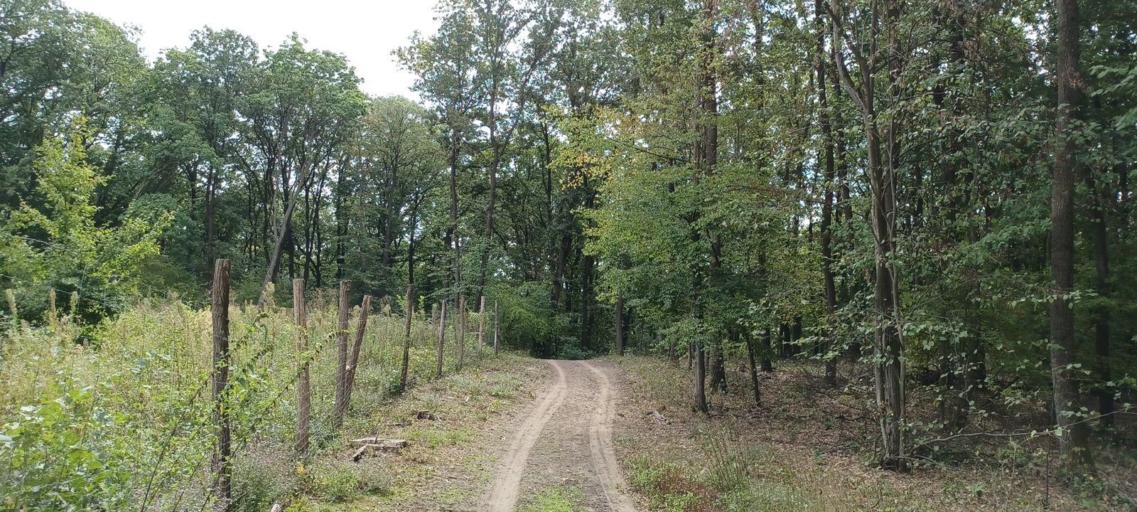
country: HU
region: Tolna
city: Szentgalpuszta
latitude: 46.3316
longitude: 18.6280
